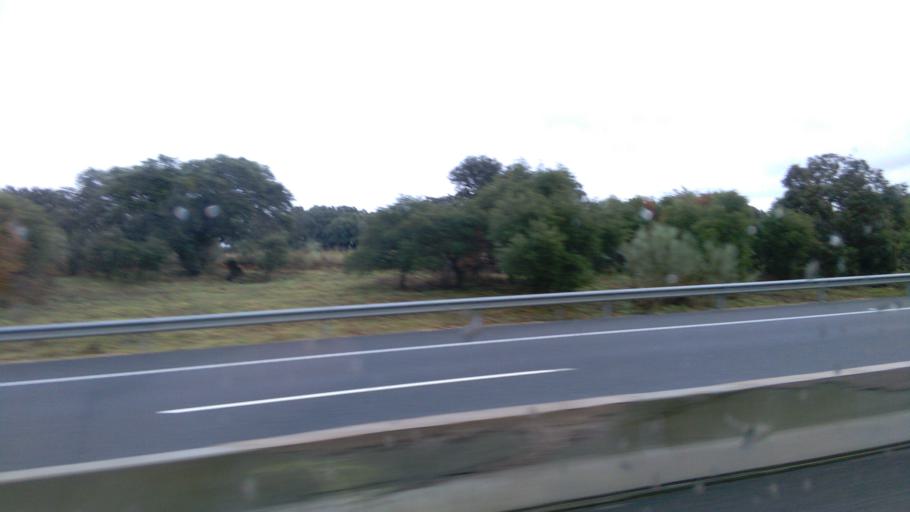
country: ES
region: Extremadura
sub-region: Provincia de Caceres
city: Casas de Miravete
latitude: 39.7656
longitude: -5.7347
